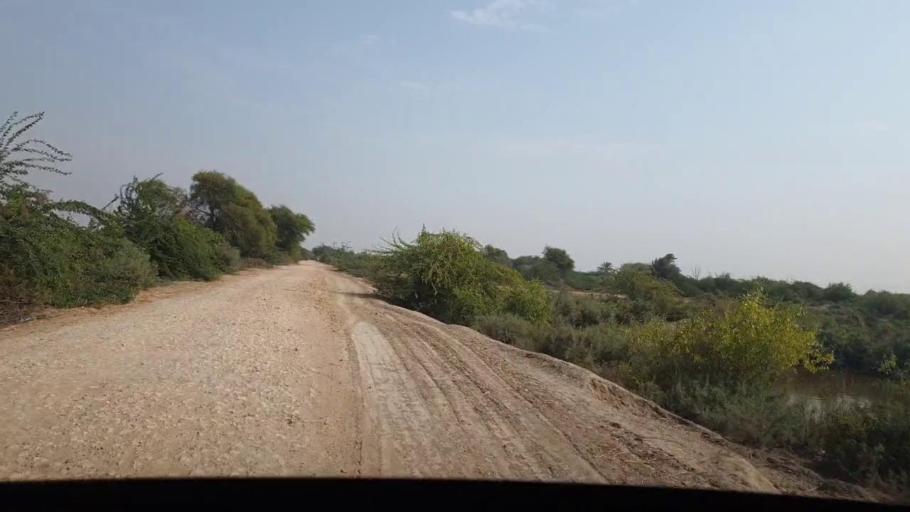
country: PK
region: Sindh
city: Chuhar Jamali
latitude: 24.2676
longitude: 67.9249
